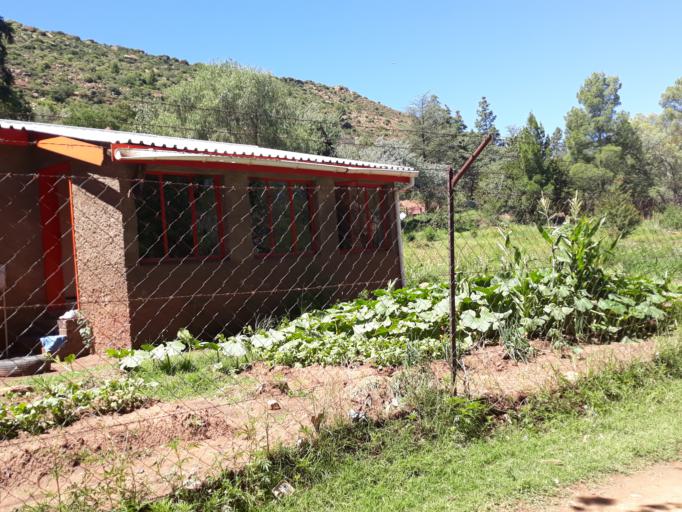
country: LS
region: Quthing
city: Quthing
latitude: -30.3409
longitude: 27.5456
